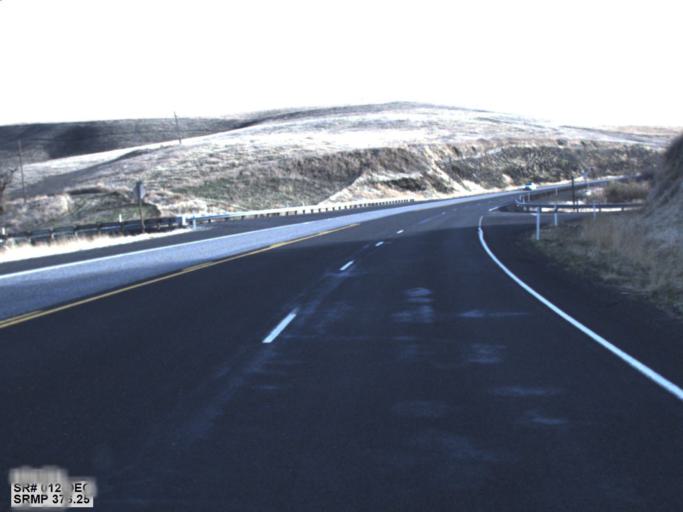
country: US
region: Washington
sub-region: Columbia County
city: Dayton
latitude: 46.4295
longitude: -117.9470
